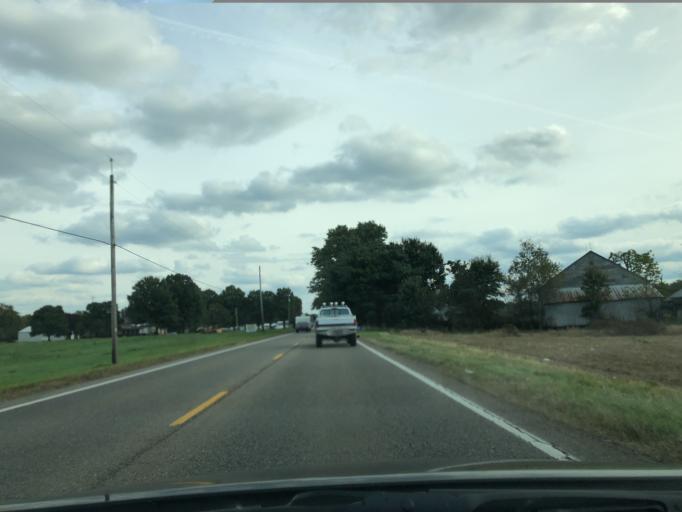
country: US
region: Ohio
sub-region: Tuscarawas County
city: Strasburg
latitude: 40.6211
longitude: -81.5429
